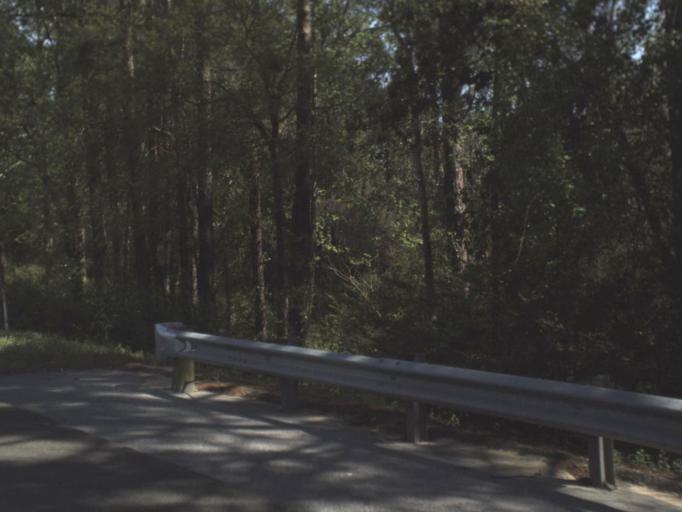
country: US
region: Florida
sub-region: Okaloosa County
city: Crestview
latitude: 30.7585
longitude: -86.5425
